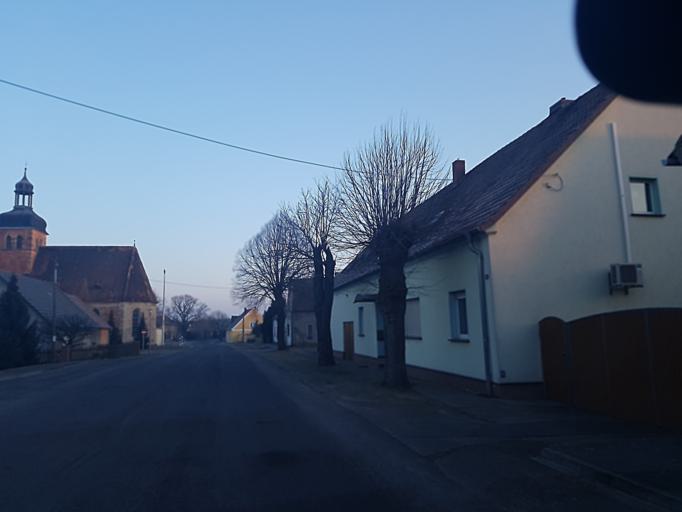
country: DE
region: Brandenburg
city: Herzberg
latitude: 51.7533
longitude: 13.2065
